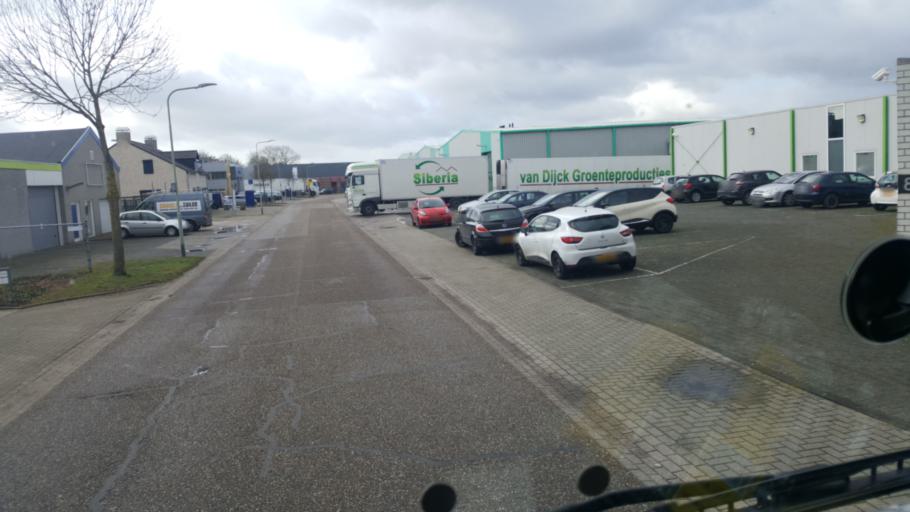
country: NL
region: Limburg
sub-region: Gemeente Venlo
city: Tegelen
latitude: 51.3189
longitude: 6.1246
